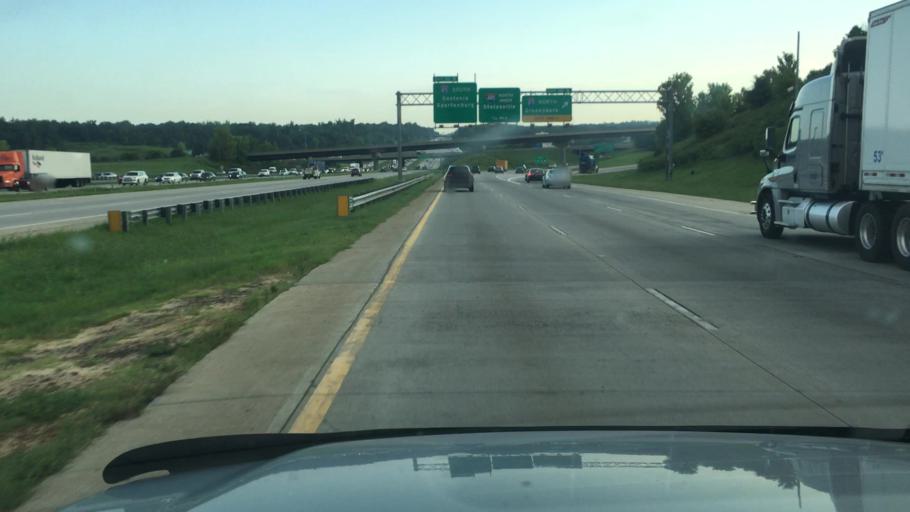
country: US
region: North Carolina
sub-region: Gaston County
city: Belmont
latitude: 35.2441
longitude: -80.9690
